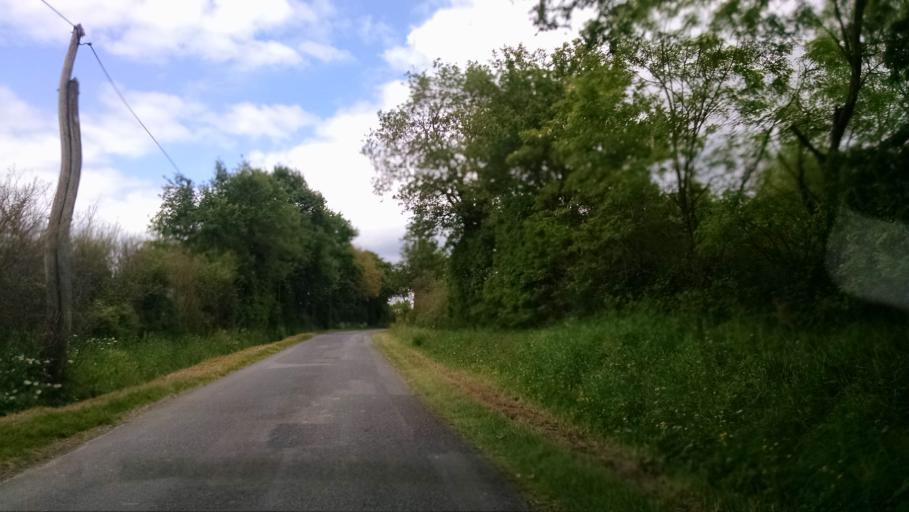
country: FR
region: Pays de la Loire
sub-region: Departement de la Loire-Atlantique
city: Remouille
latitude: 47.0342
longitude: -1.3843
